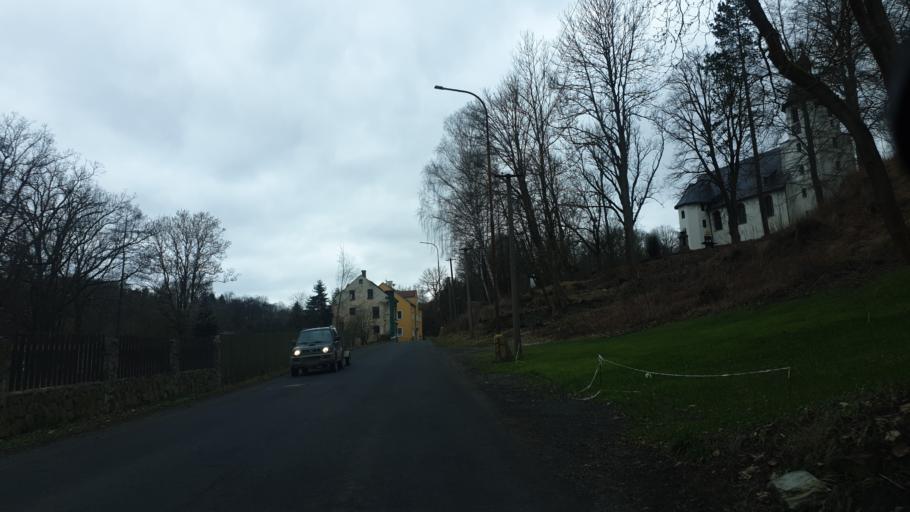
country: CZ
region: Karlovarsky
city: As
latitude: 50.2548
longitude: 12.2055
